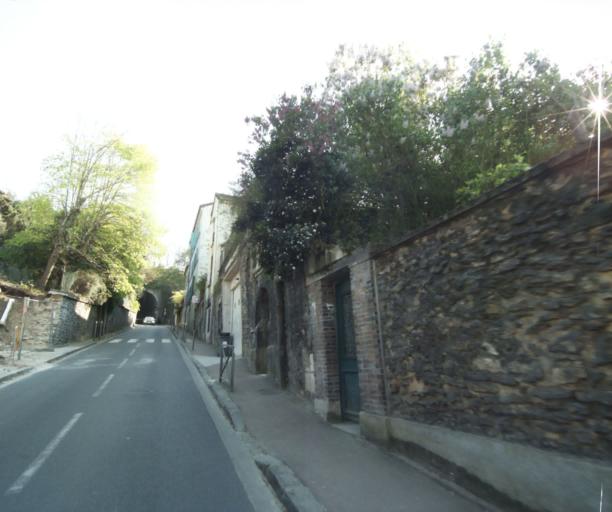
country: FR
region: Ile-de-France
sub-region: Departement des Hauts-de-Seine
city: Sevres
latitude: 48.8220
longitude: 2.2121
